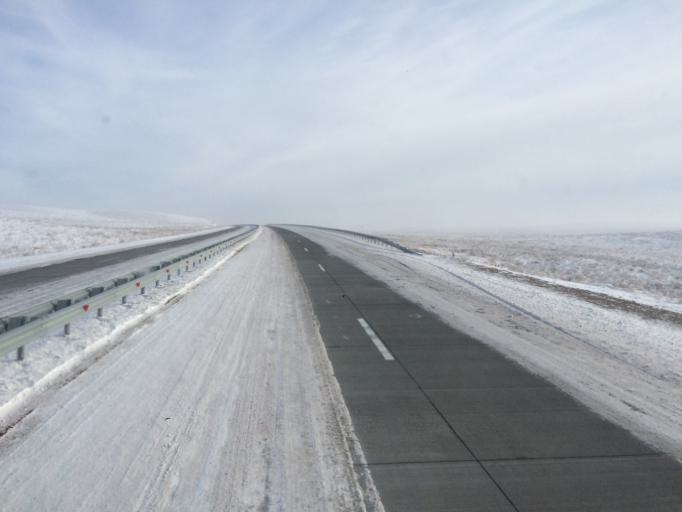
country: KZ
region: Zhambyl
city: Georgiyevka
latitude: 43.3397
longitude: 74.4596
